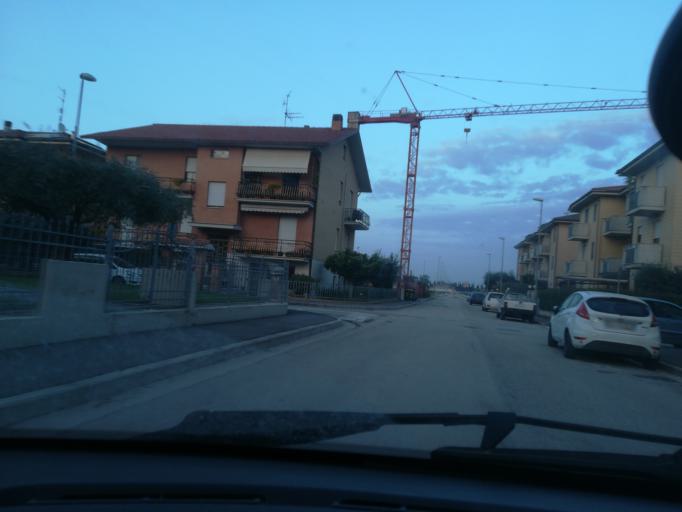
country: IT
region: The Marches
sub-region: Provincia di Macerata
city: Piediripa
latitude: 43.2743
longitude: 13.5030
